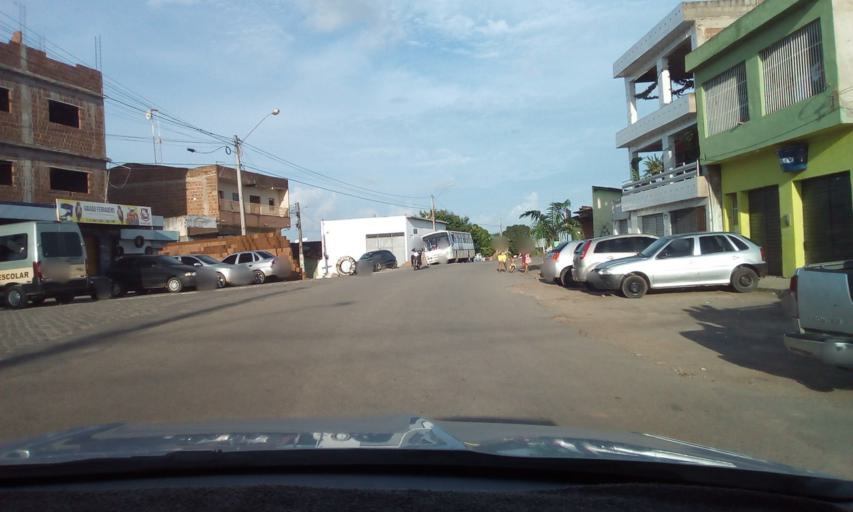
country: BR
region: Pernambuco
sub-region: Gloria Do Goita
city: Gloria do Goita
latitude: -7.9949
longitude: -35.2127
